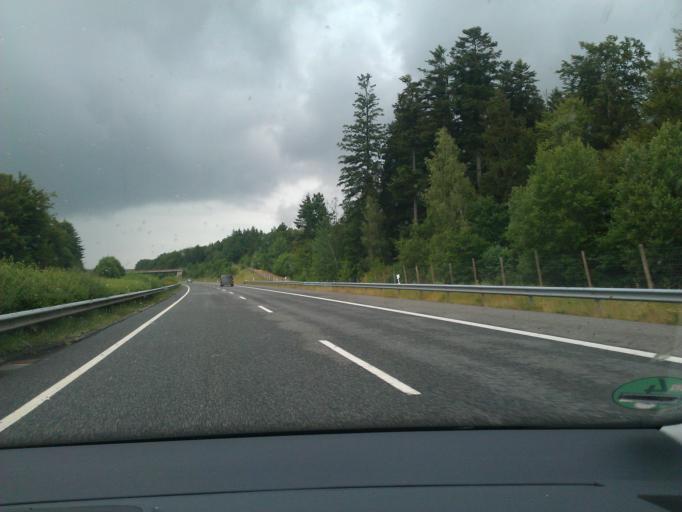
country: DE
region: Rheinland-Pfalz
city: Gindorf
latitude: 50.0185
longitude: 6.6617
